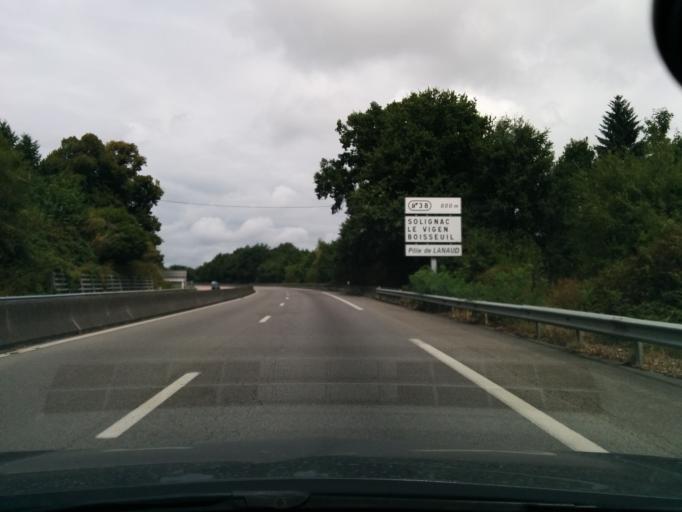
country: FR
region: Limousin
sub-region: Departement de la Haute-Vienne
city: Boisseuil
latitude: 45.7450
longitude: 1.3405
